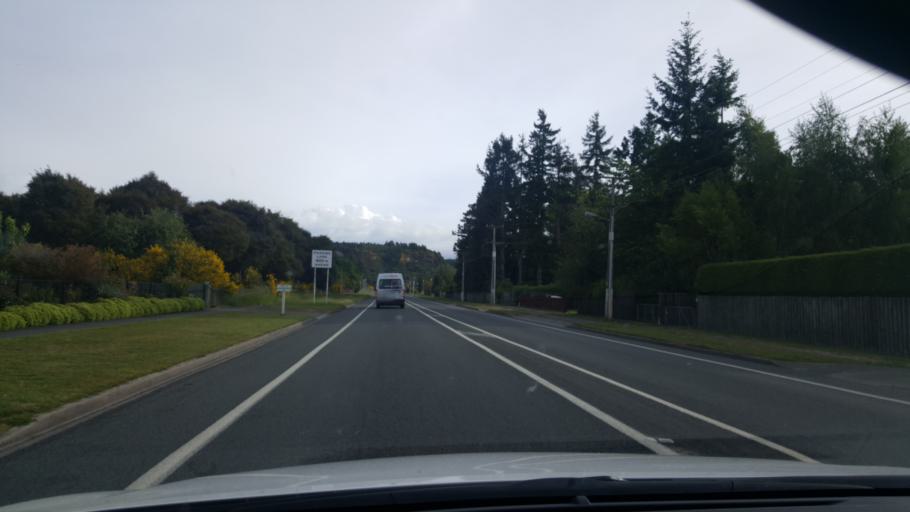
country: NZ
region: Waikato
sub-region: Taupo District
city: Taupo
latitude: -38.7927
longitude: 176.0759
